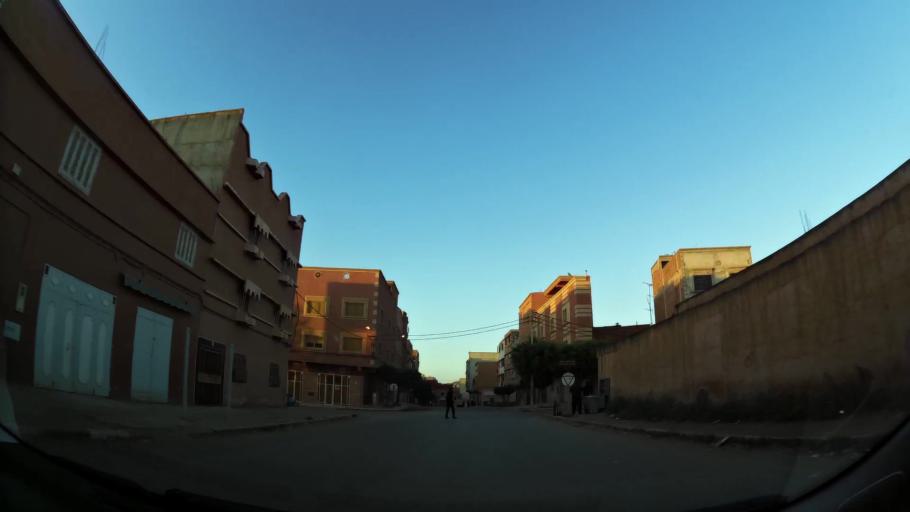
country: MA
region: Oriental
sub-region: Berkane-Taourirt
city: Berkane
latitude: 34.9168
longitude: -2.3144
